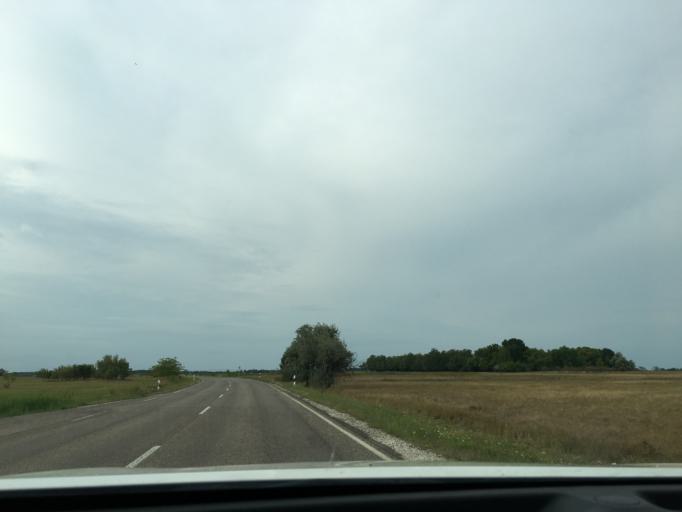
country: HU
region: Hajdu-Bihar
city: Egyek
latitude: 47.5685
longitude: 20.8609
